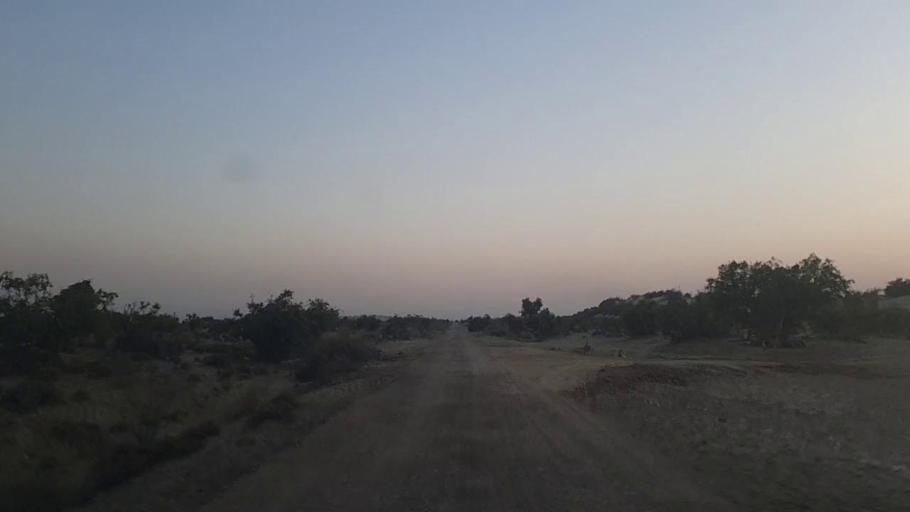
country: PK
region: Sindh
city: Jam Sahib
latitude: 26.4134
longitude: 68.8094
